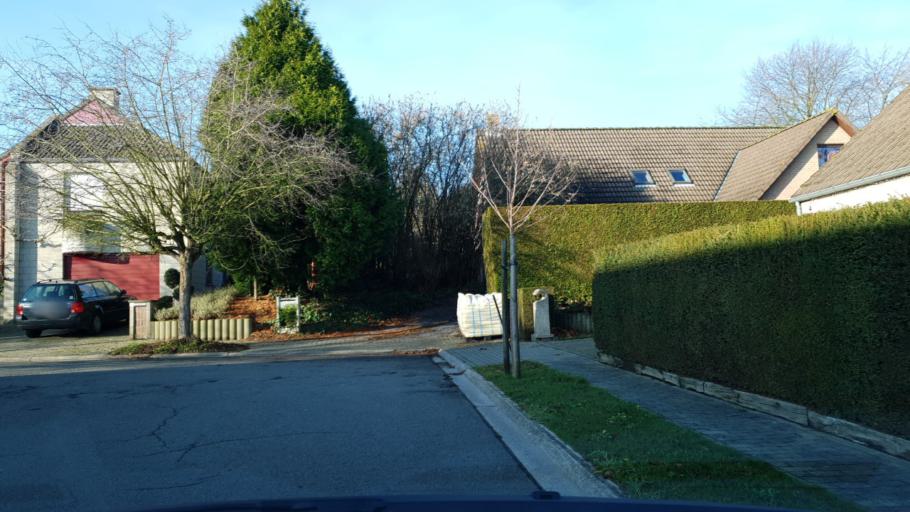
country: BE
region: Flanders
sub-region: Provincie Vlaams-Brabant
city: Herent
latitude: 50.8865
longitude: 4.6607
